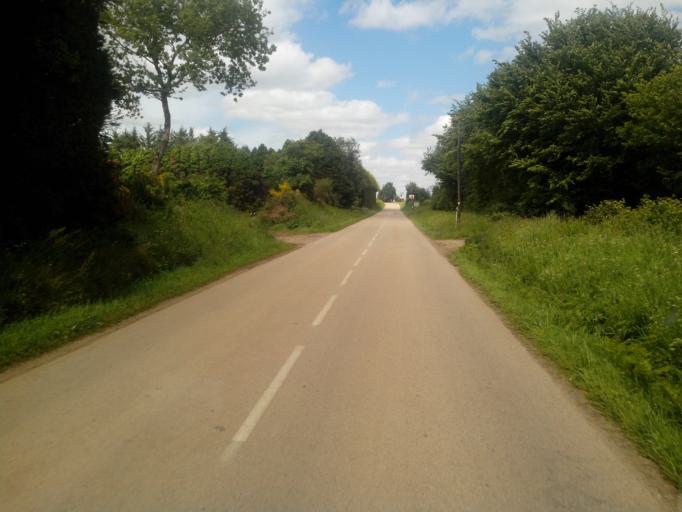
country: FR
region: Brittany
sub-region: Departement du Finistere
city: Guerlesquin
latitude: 48.5040
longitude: -3.6078
